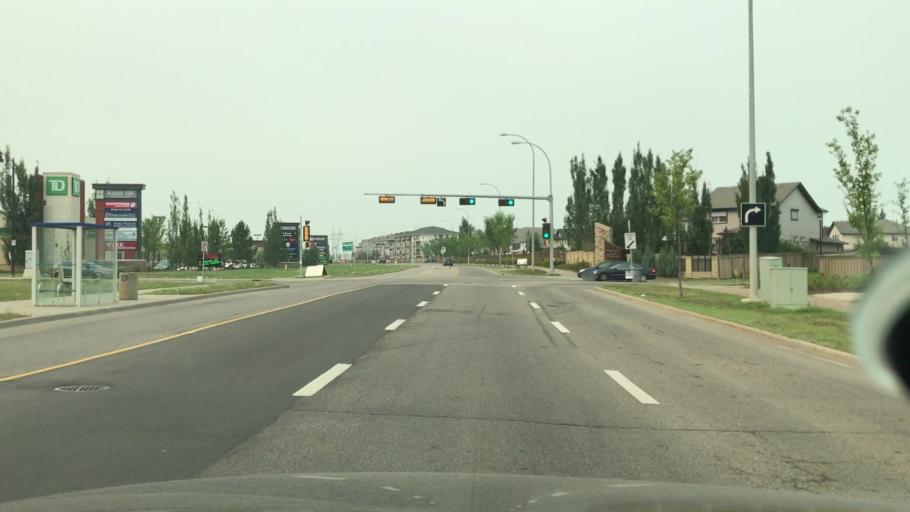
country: CA
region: Alberta
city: Edmonton
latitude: 53.4365
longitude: -113.5708
